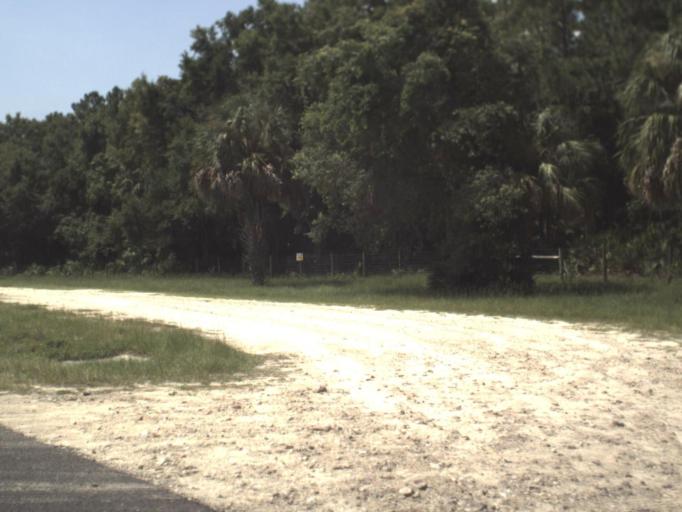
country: US
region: Florida
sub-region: Levy County
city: Inglis
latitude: 29.0177
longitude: -82.6670
